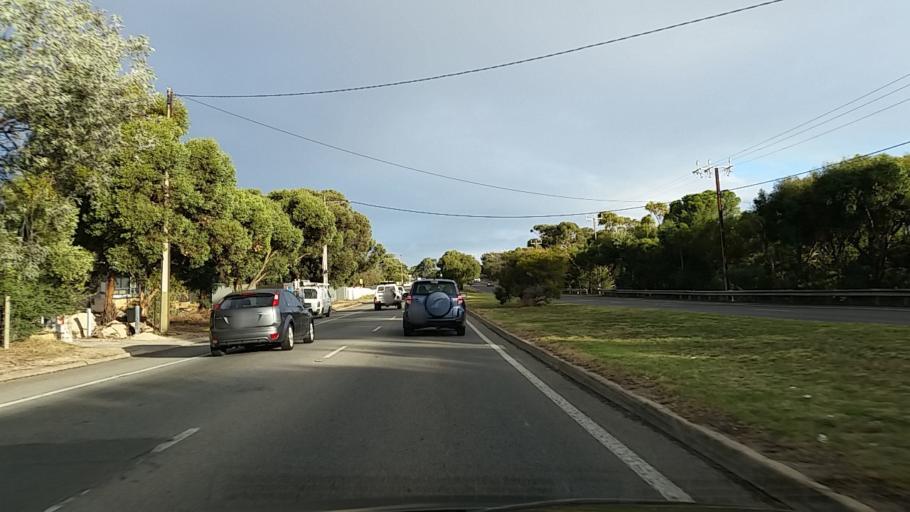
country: AU
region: South Australia
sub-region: Adelaide Hills
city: Seacliff
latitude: -35.0446
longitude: 138.5313
